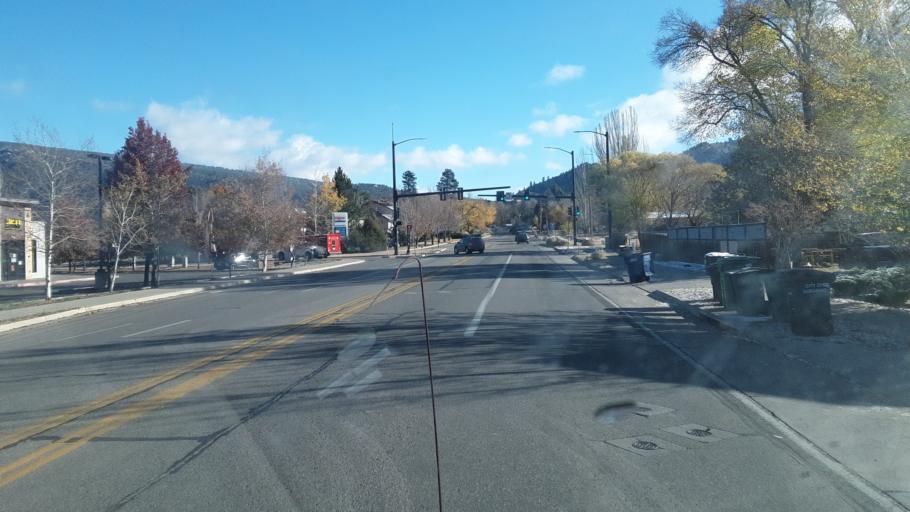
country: US
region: Colorado
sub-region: La Plata County
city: Durango
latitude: 37.2972
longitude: -107.8496
